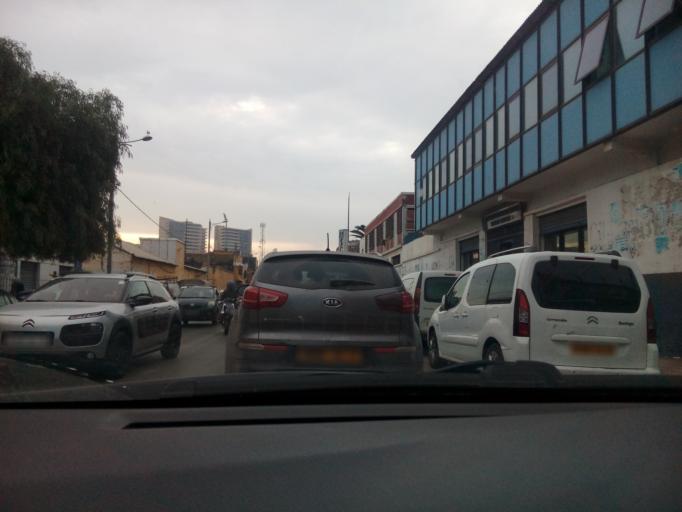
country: DZ
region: Oran
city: Oran
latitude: 35.6850
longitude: -0.6398
